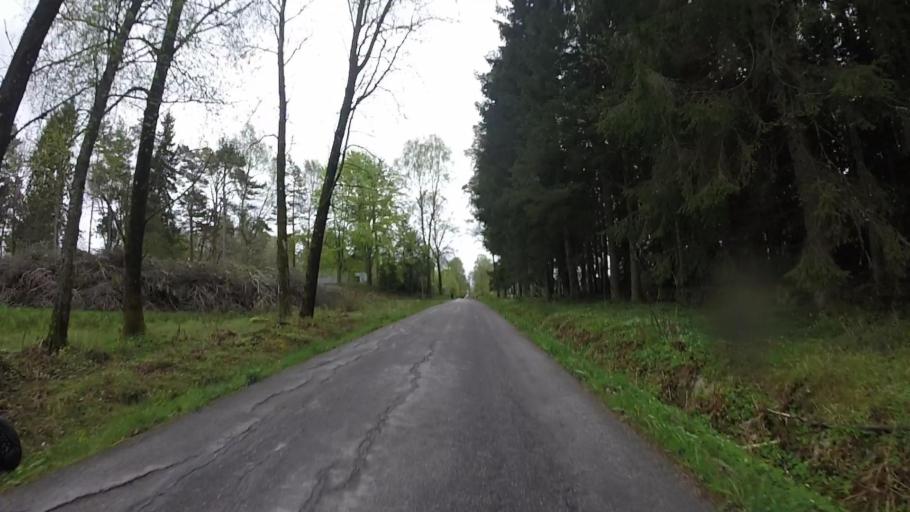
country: SE
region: Vaestra Goetaland
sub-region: Trollhattan
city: Sjuntorp
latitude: 58.2040
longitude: 12.2114
